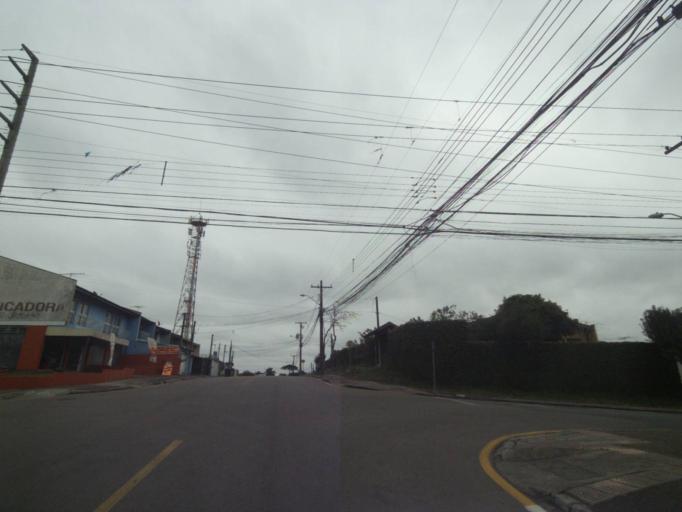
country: BR
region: Parana
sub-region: Sao Jose Dos Pinhais
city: Sao Jose dos Pinhais
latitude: -25.4860
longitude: -49.2284
